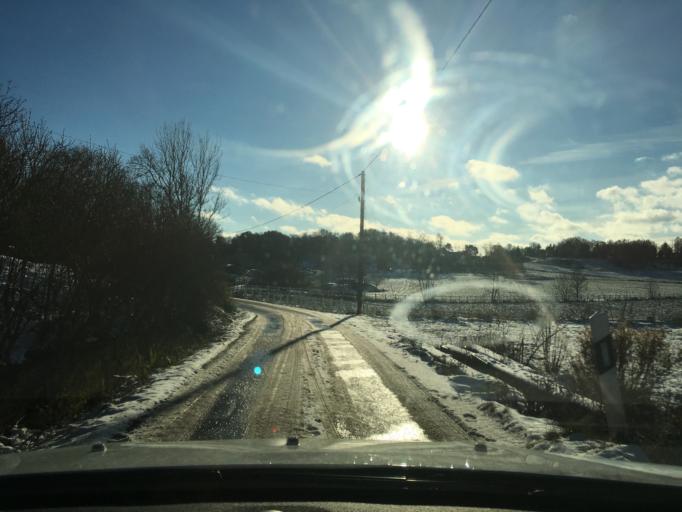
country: SE
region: Vaestra Goetaland
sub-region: Tjorns Kommun
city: Myggenas
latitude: 58.0939
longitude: 11.7694
